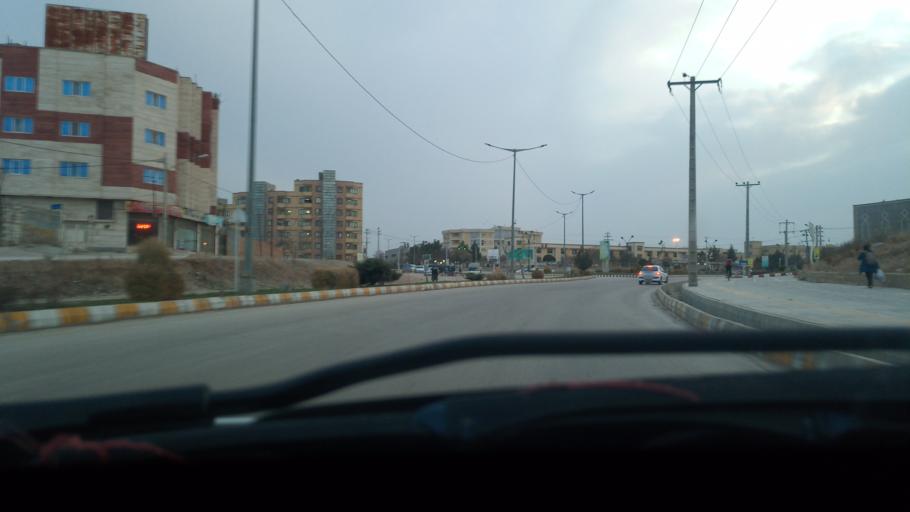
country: IR
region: Khorasan-e Shomali
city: Bojnurd
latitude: 37.4547
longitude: 57.3278
